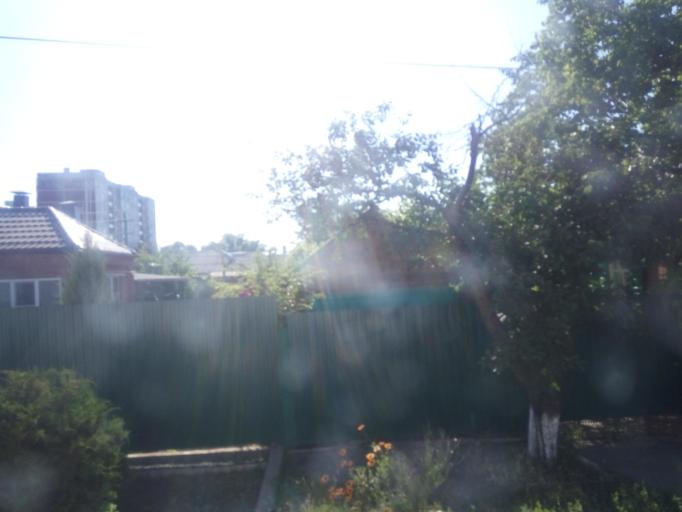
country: RU
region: Rostov
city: Bataysk
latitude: 47.1214
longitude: 39.7353
